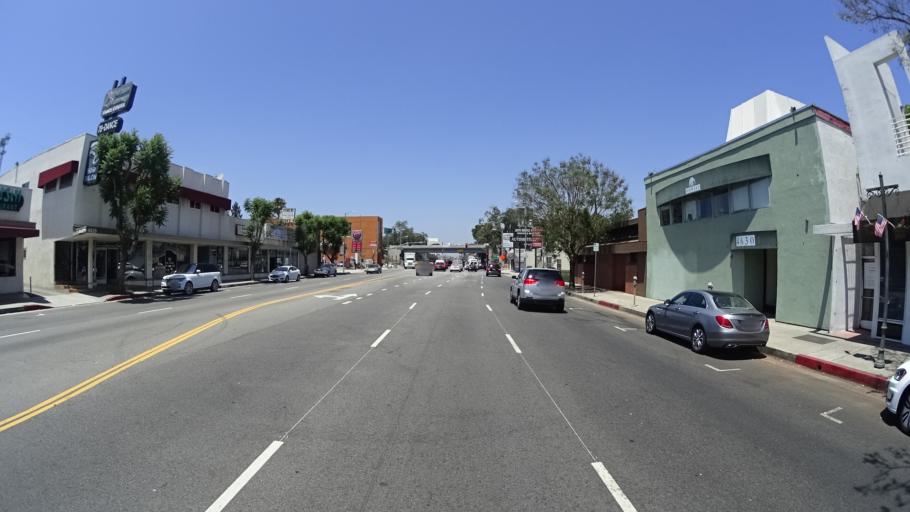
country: US
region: California
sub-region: Los Angeles County
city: Sherman Oaks
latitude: 34.1555
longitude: -118.4486
